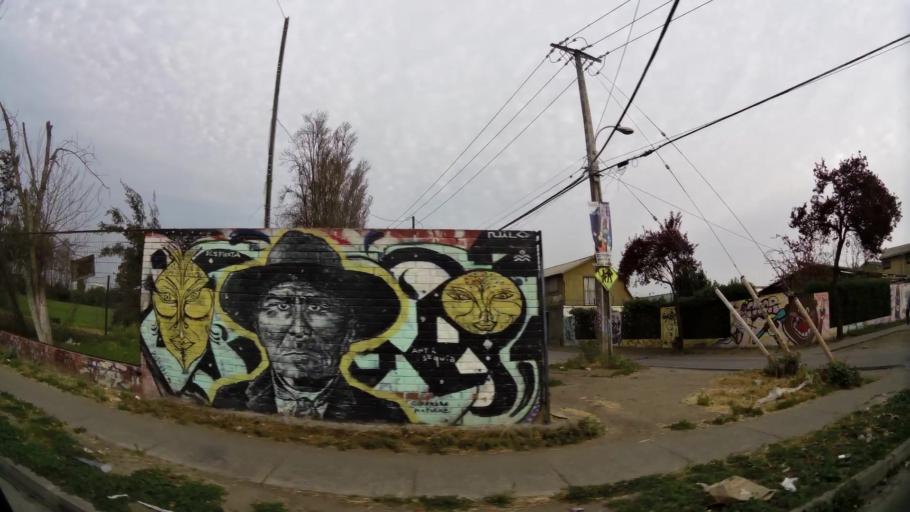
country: CL
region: Santiago Metropolitan
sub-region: Provincia de Maipo
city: San Bernardo
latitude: -33.5289
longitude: -70.7704
